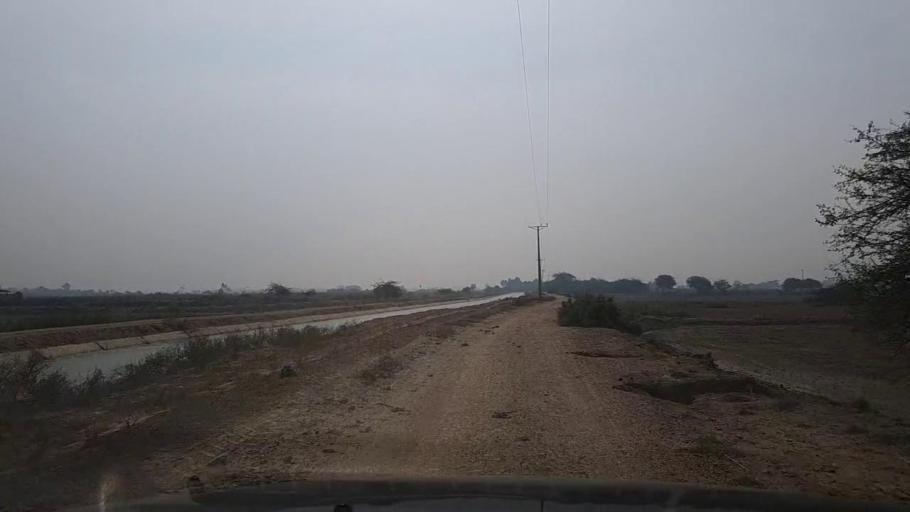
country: PK
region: Sindh
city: Mirpur Sakro
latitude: 24.5289
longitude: 67.8112
